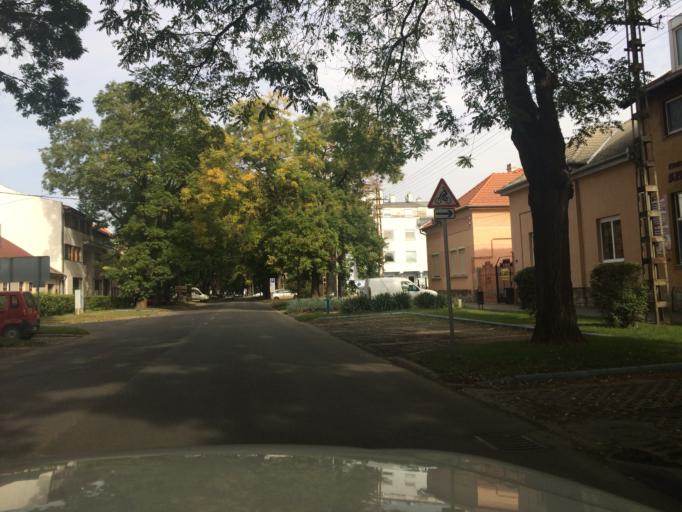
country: HU
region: Szabolcs-Szatmar-Bereg
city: Nyiregyhaza
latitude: 47.9494
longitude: 21.7157
